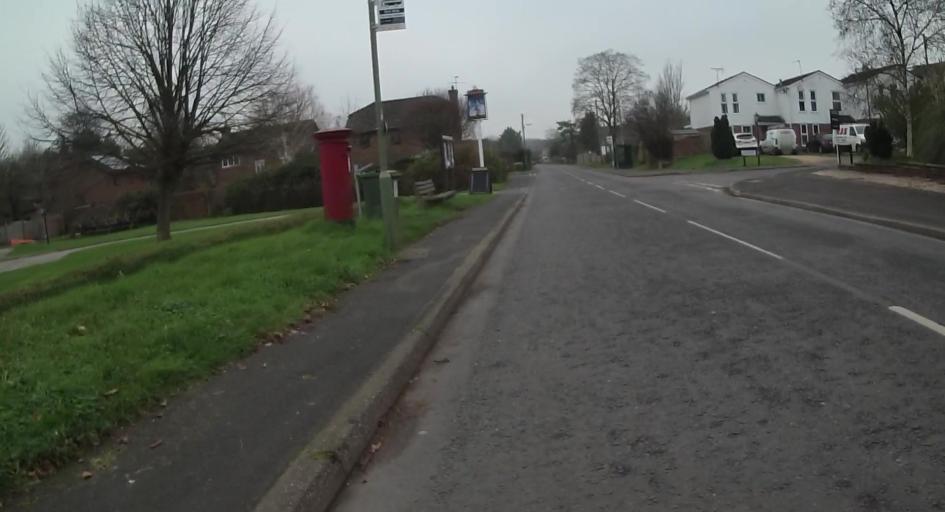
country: GB
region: England
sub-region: Hampshire
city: Kings Worthy
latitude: 51.1071
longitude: -1.3030
